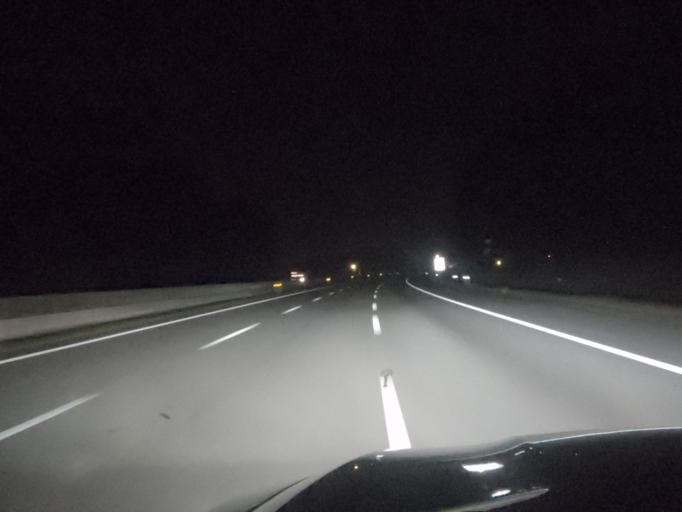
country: PT
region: Aveiro
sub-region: Estarreja
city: Avanca
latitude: 40.7944
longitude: -8.5494
